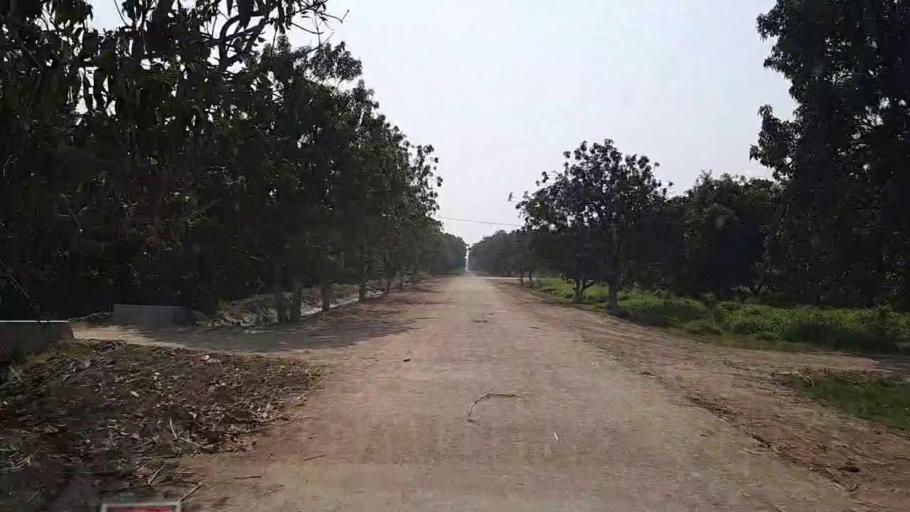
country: PK
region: Sindh
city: Mirwah Gorchani
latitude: 25.3250
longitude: 69.0075
